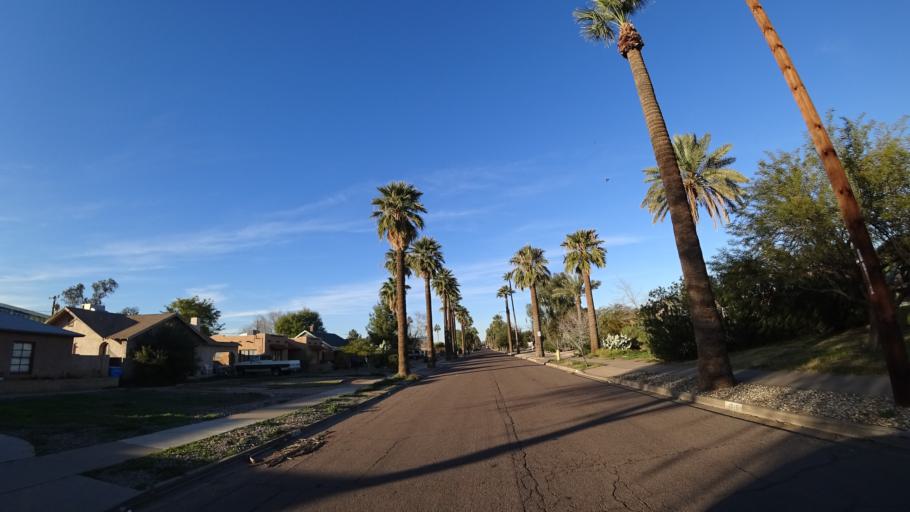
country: US
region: Arizona
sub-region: Maricopa County
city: Phoenix
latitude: 33.4681
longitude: -112.0938
